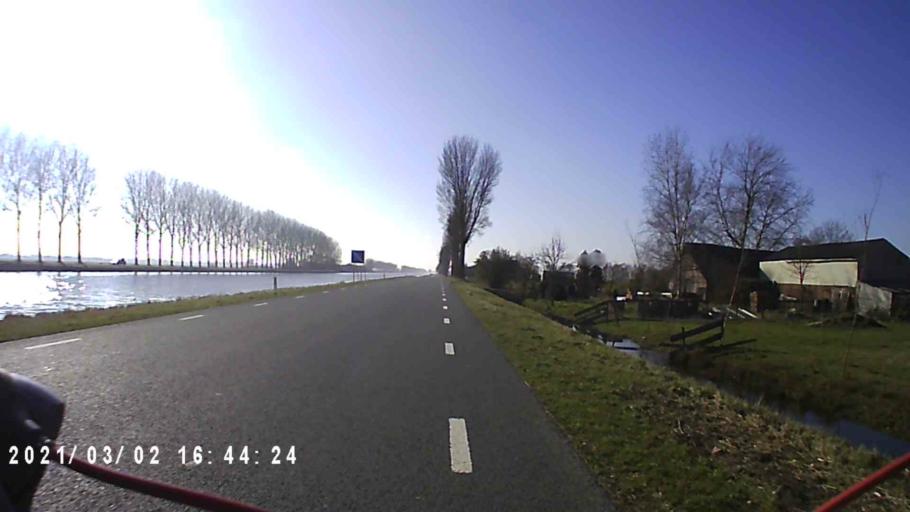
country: NL
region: Groningen
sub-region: Gemeente Zuidhorn
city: Grijpskerk
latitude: 53.2477
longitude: 6.2959
